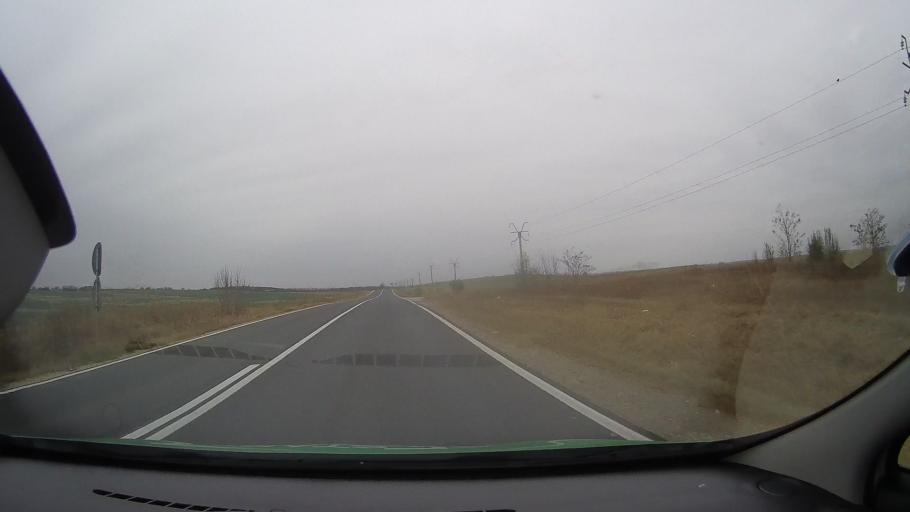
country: RO
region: Constanta
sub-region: Oras Harsova
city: Harsova
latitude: 44.6936
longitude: 27.9383
